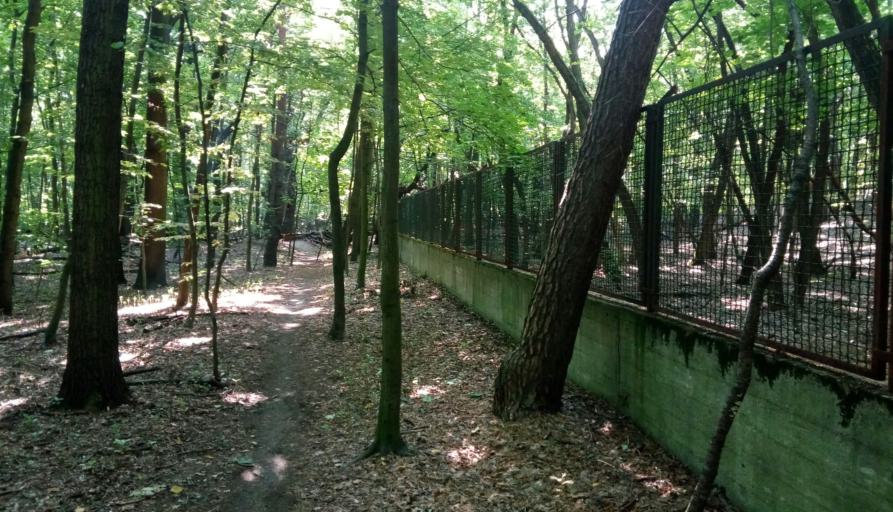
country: PL
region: Masovian Voivodeship
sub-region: Warszawa
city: Bielany
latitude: 52.2873
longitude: 20.9634
